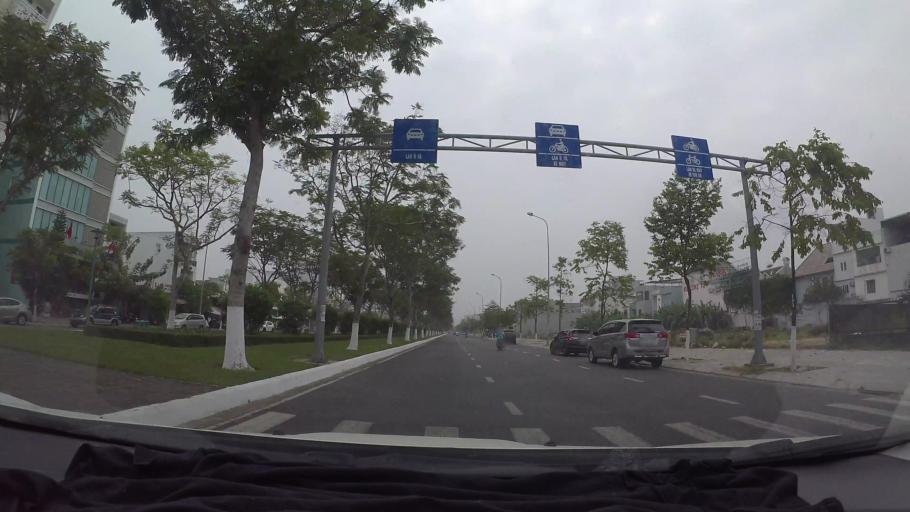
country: VN
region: Da Nang
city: Cam Le
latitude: 16.0396
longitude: 108.2122
